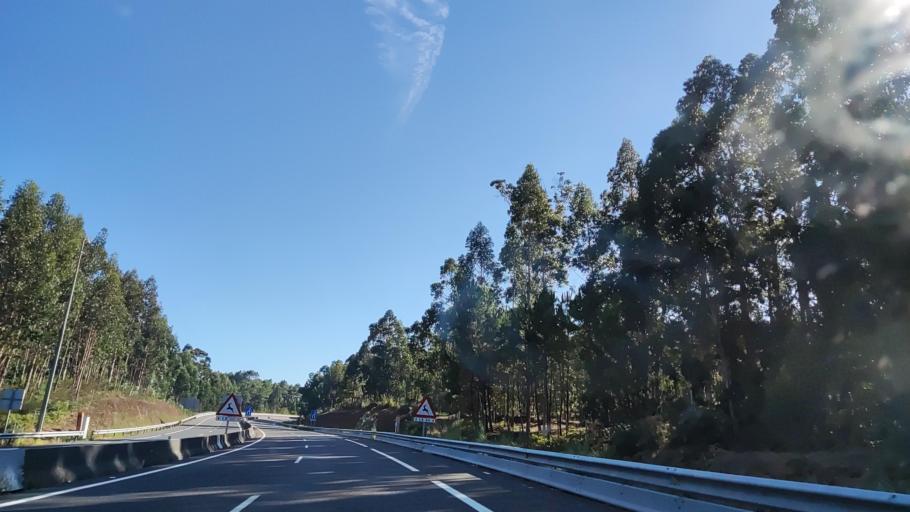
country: ES
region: Galicia
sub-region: Provincia da Coruna
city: Boiro
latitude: 42.5810
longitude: -8.9877
